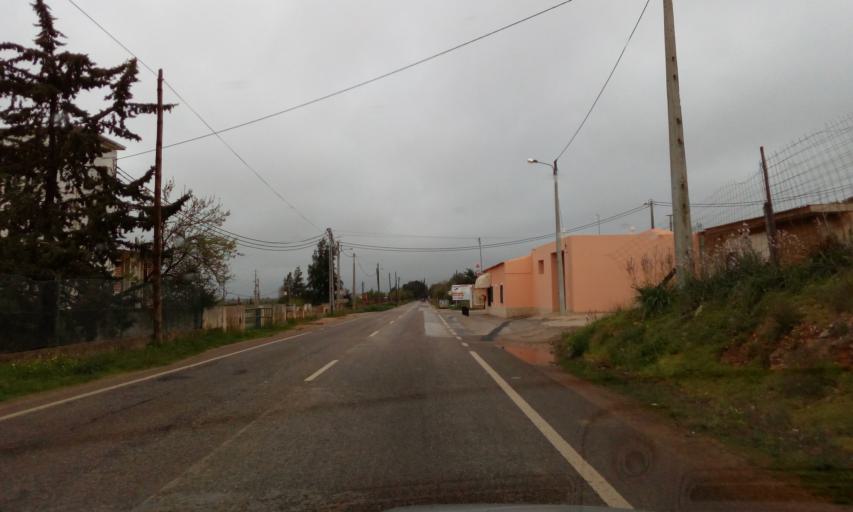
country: PT
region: Faro
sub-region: Silves
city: Armacao de Pera
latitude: 37.1678
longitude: -8.3564
